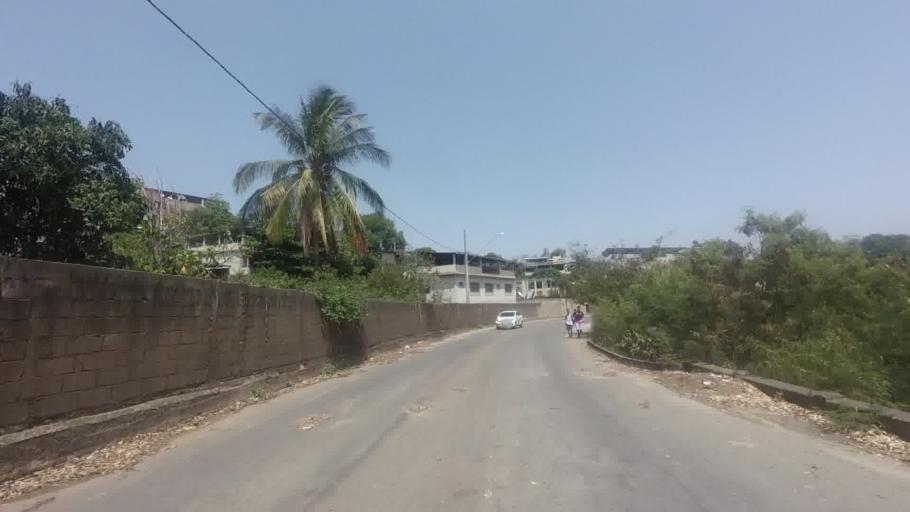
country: BR
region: Espirito Santo
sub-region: Cachoeiro De Itapemirim
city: Cachoeiro de Itapemirim
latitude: -20.8492
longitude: -41.1474
